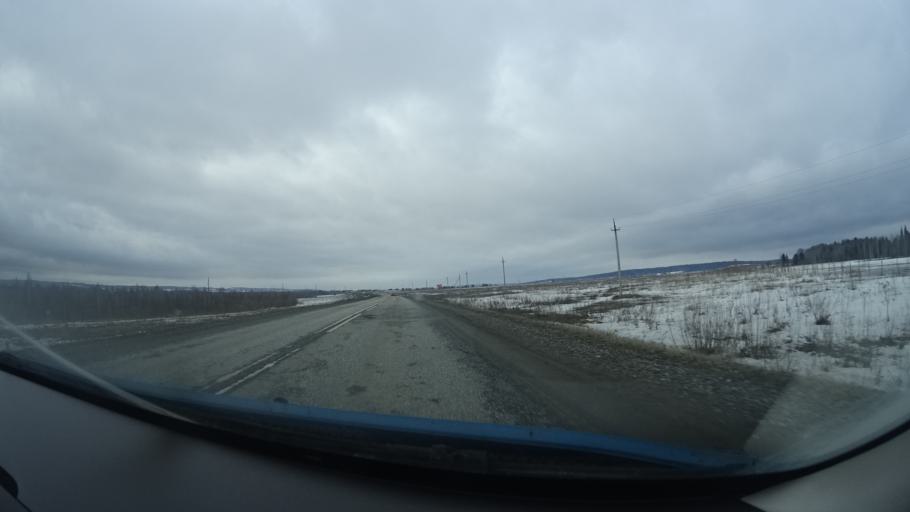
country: RU
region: Perm
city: Barda
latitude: 56.9639
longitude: 55.5791
